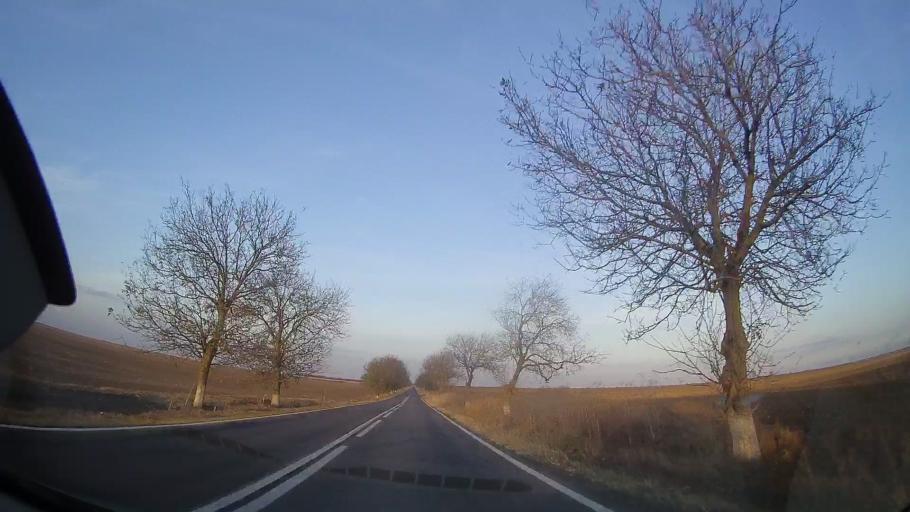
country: RO
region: Constanta
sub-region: Comuna Topraisar
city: Topraisar
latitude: 43.9881
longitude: 28.4222
